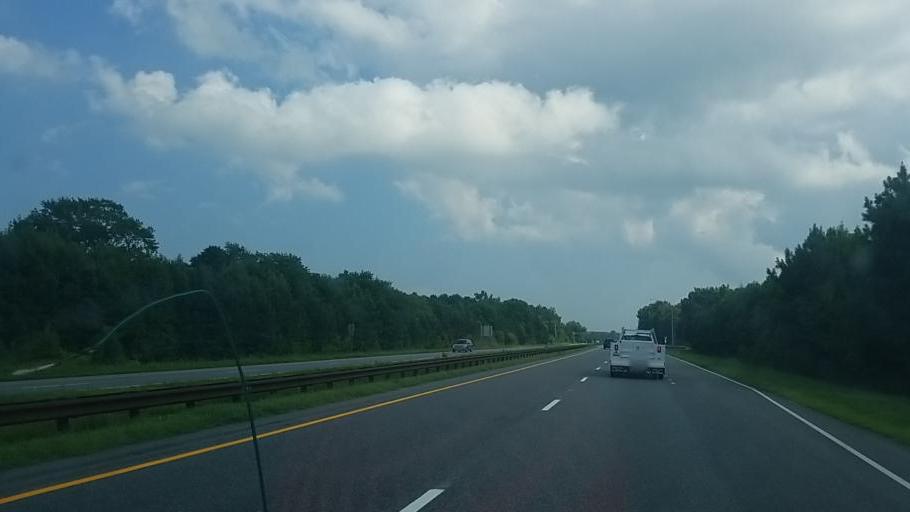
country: US
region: Delaware
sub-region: Sussex County
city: Selbyville
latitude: 38.4389
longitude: -75.2253
